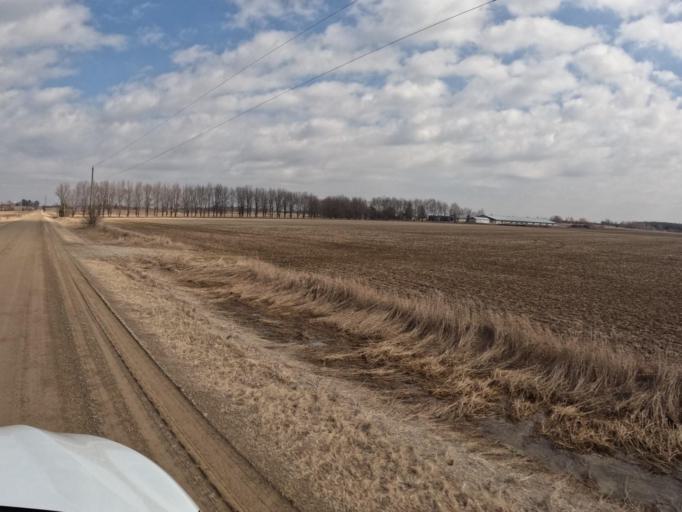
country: CA
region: Ontario
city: Orangeville
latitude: 43.9240
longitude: -80.2402
